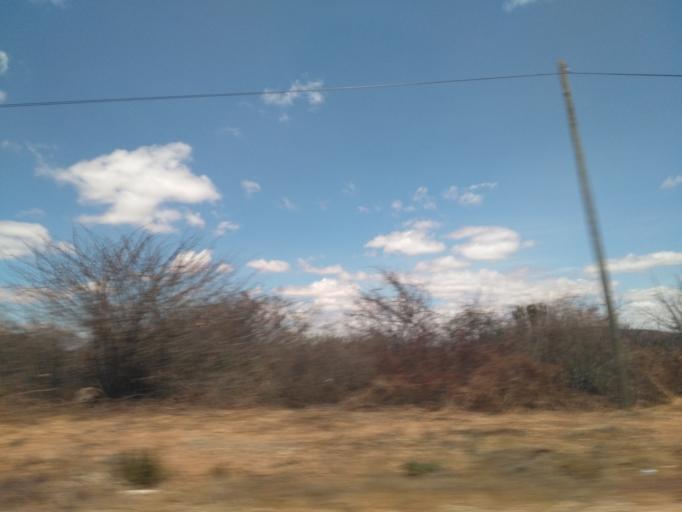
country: TZ
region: Dodoma
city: Kisasa
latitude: -6.2199
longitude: 35.8134
